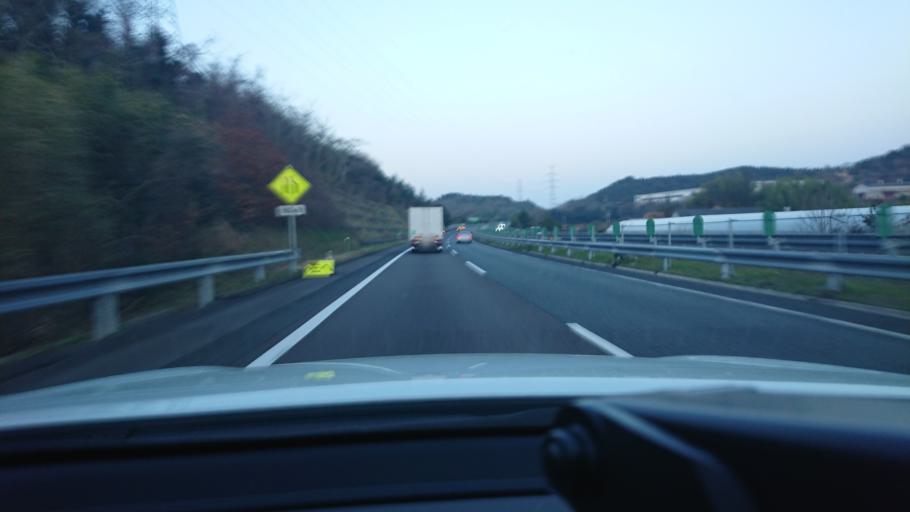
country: JP
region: Kagawa
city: Takamatsu-shi
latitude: 34.2699
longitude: 133.9481
